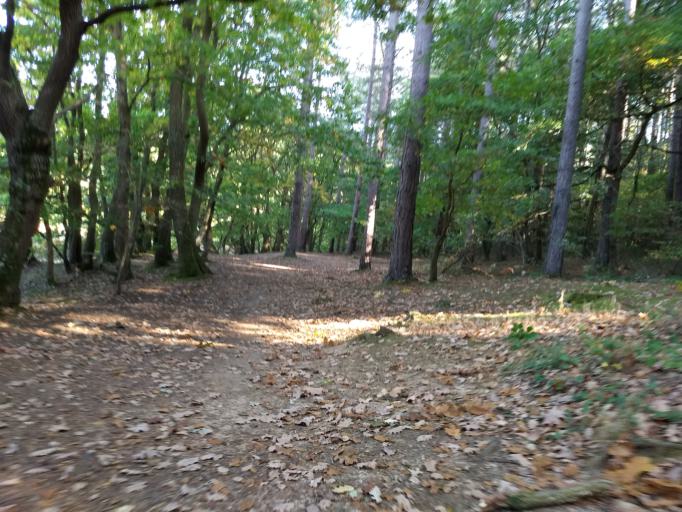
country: GB
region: England
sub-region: Isle of Wight
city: Newchurch
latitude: 50.7158
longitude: -1.2199
